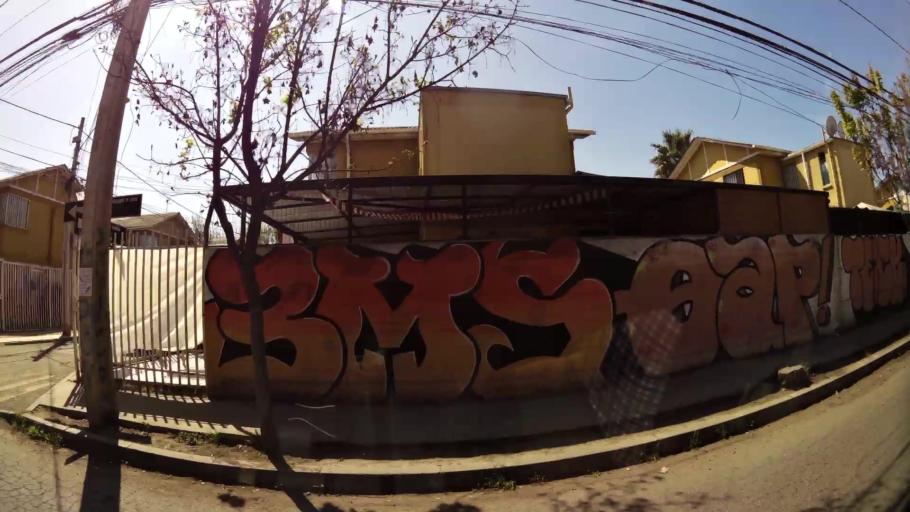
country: CL
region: Santiago Metropolitan
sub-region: Provincia de Santiago
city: Lo Prado
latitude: -33.3552
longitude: -70.7174
